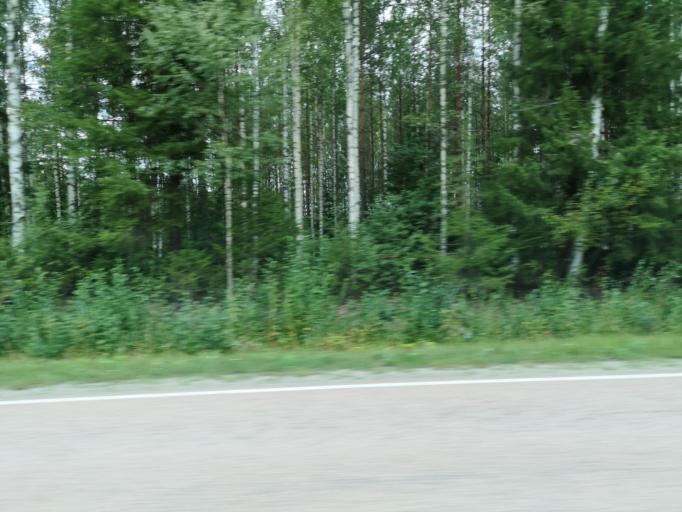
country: FI
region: Central Finland
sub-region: Jyvaeskylae
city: Hankasalmi
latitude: 62.3595
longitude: 26.5514
